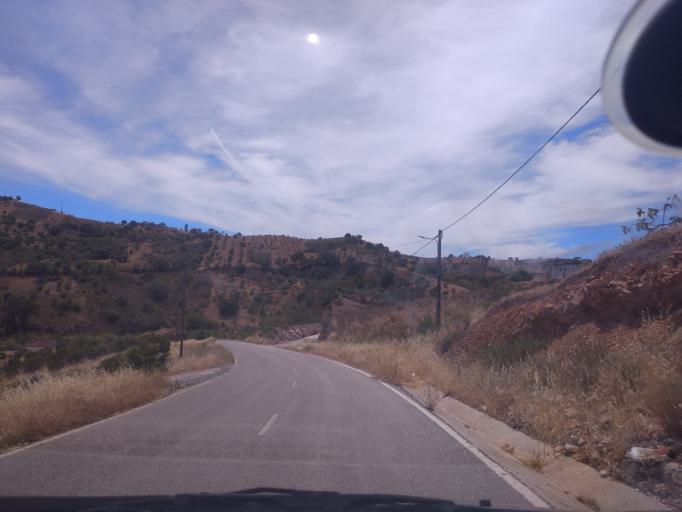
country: PT
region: Faro
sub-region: Sao Bras de Alportel
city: Sao Bras de Alportel
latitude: 37.1797
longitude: -7.8001
